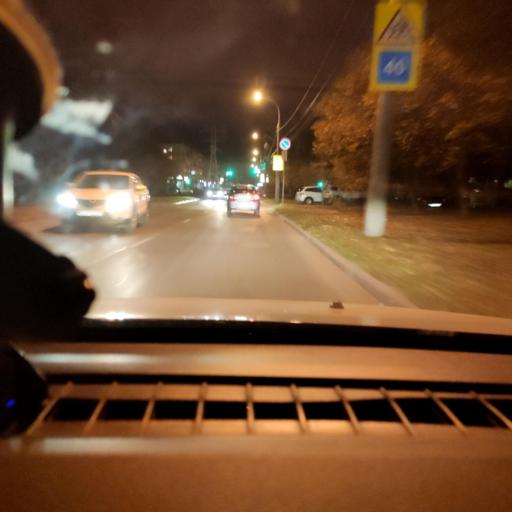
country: RU
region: Samara
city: Samara
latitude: 53.1978
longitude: 50.1712
